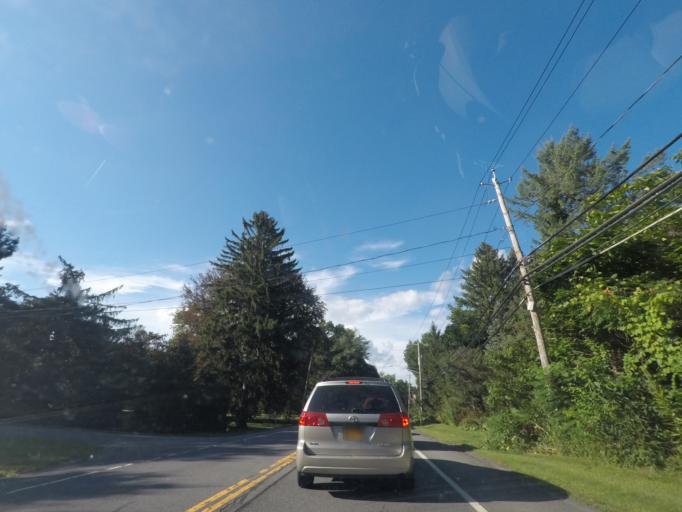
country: US
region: New York
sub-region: Albany County
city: West Albany
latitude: 42.6901
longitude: -73.7528
